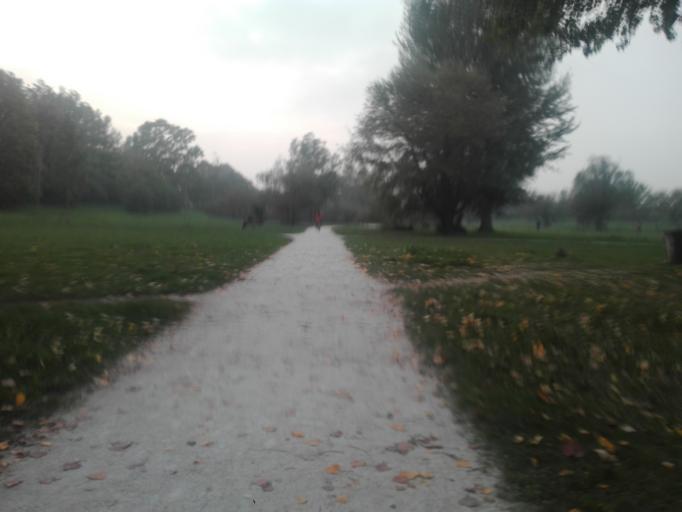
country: IT
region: Emilia-Romagna
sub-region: Provincia di Rimini
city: Rimini
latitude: 44.0632
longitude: 12.5554
